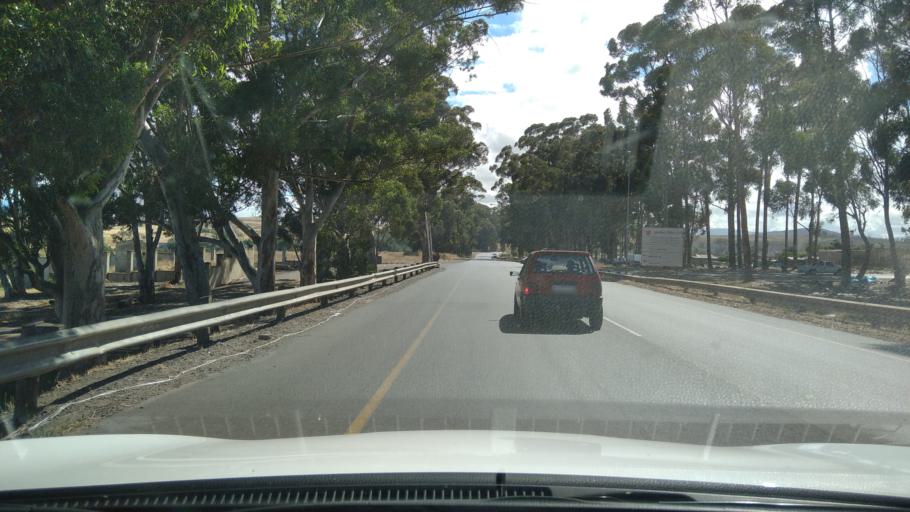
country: ZA
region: Western Cape
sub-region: City of Cape Town
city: Kraaifontein
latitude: -33.7815
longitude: 18.7144
